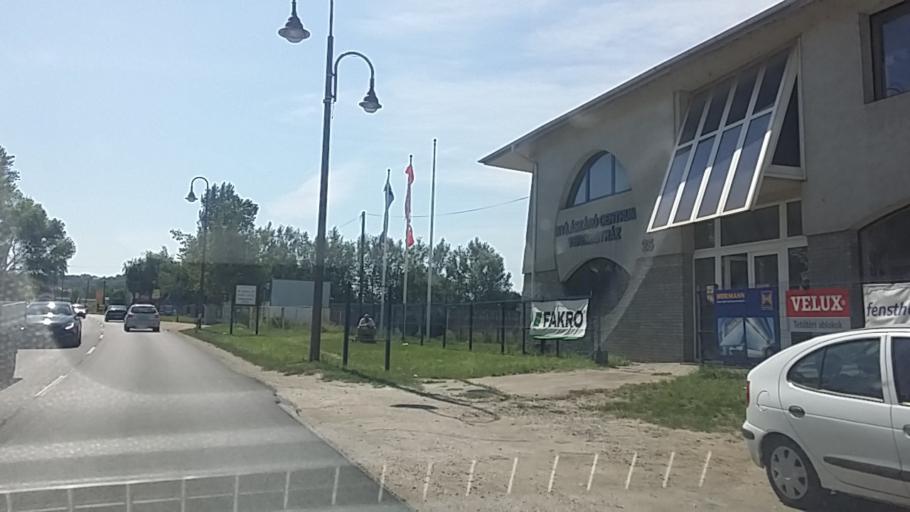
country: HU
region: Pest
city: Veresegyhaz
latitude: 47.6440
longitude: 19.2972
